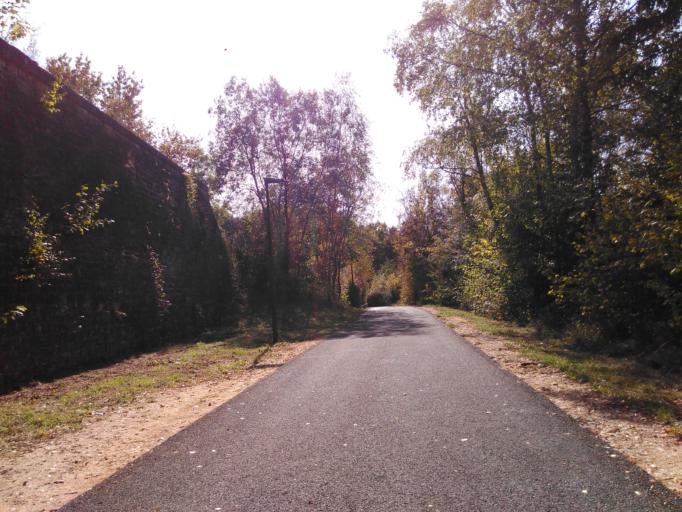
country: LU
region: Luxembourg
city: Tetange
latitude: 49.4695
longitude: 6.0384
